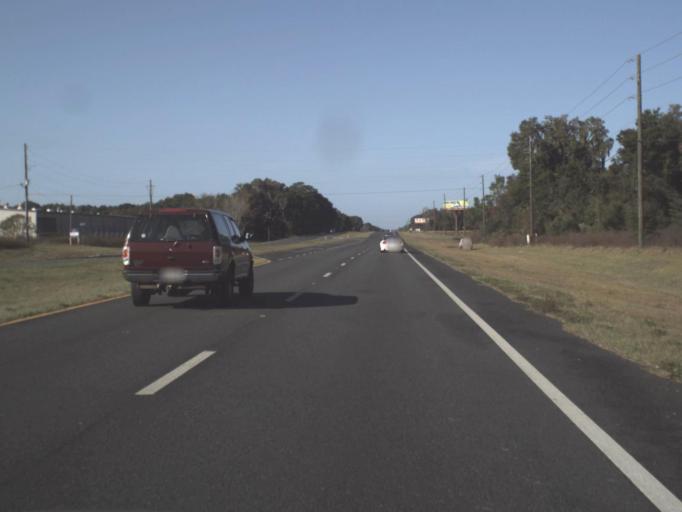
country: US
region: Florida
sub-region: Marion County
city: Belleview
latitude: 29.0261
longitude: -82.0928
